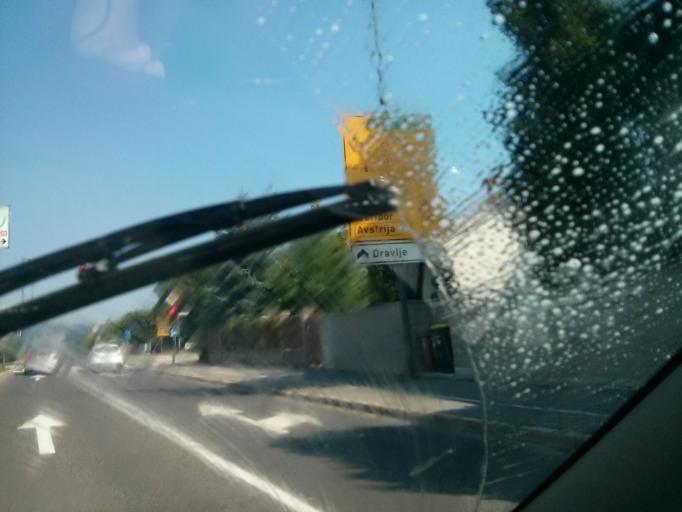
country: SI
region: Ljubljana
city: Ljubljana
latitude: 46.0761
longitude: 14.4740
